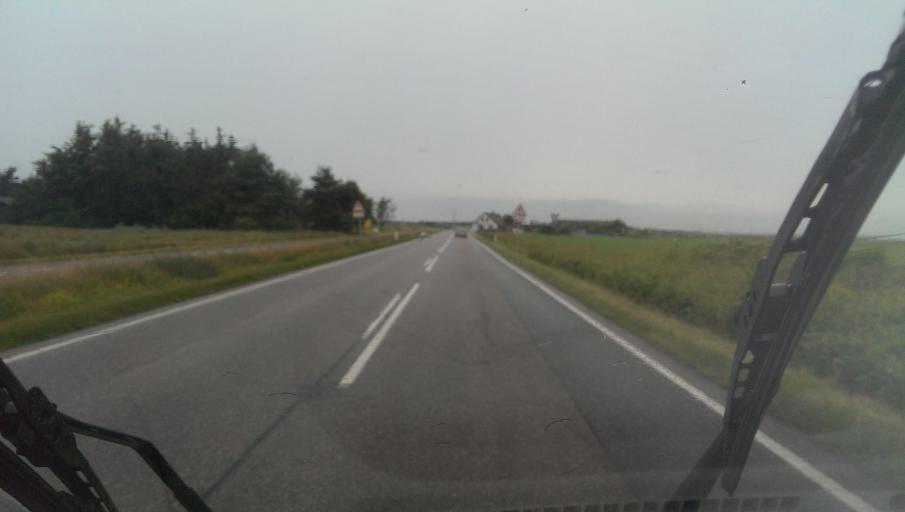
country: DK
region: Central Jutland
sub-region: Ringkobing-Skjern Kommune
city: Hvide Sande
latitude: 56.0780
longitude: 8.1202
